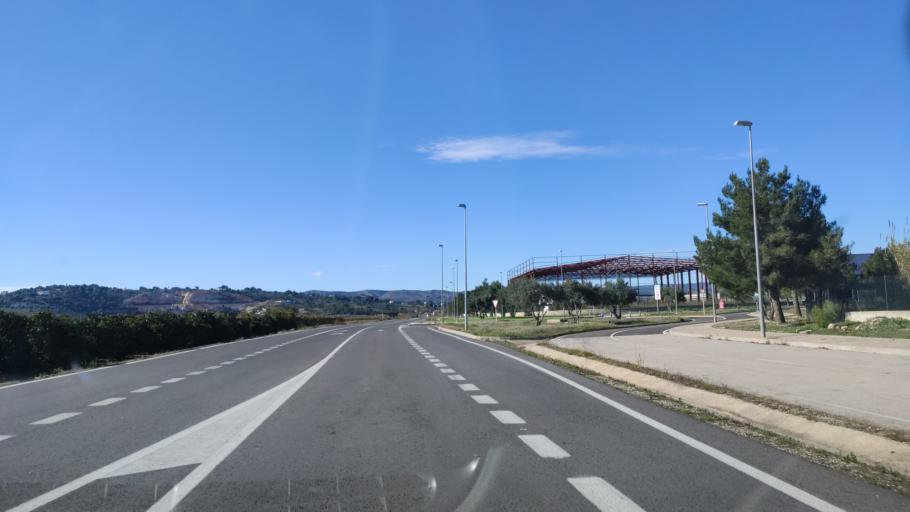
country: ES
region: Valencia
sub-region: Provincia de Valencia
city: Alberic
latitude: 39.1201
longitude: -0.5370
